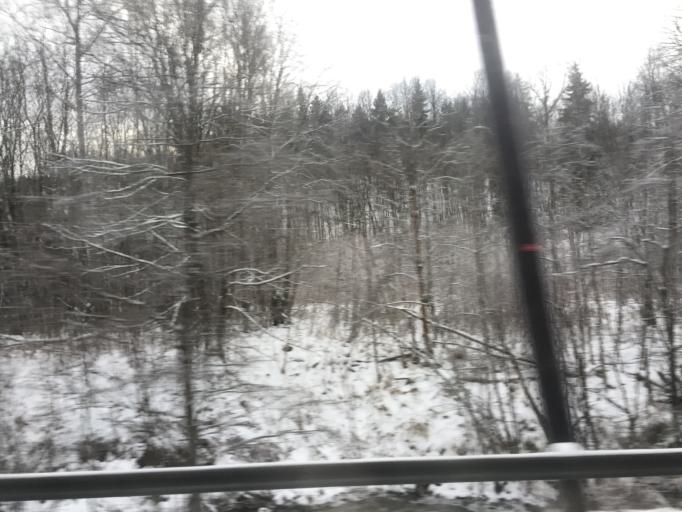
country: NO
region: Akershus
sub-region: As
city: As
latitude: 59.7186
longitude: 10.7292
